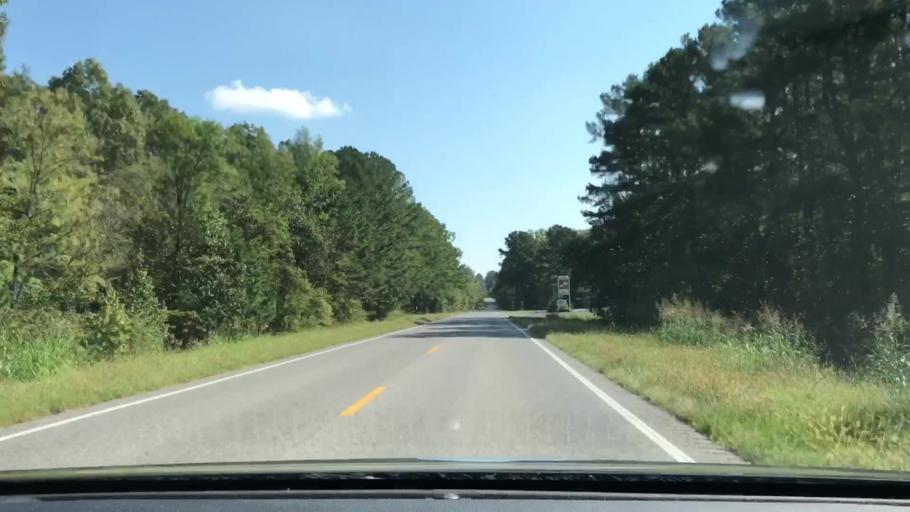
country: US
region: Kentucky
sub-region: Marshall County
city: Benton
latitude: 36.7646
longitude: -88.2293
